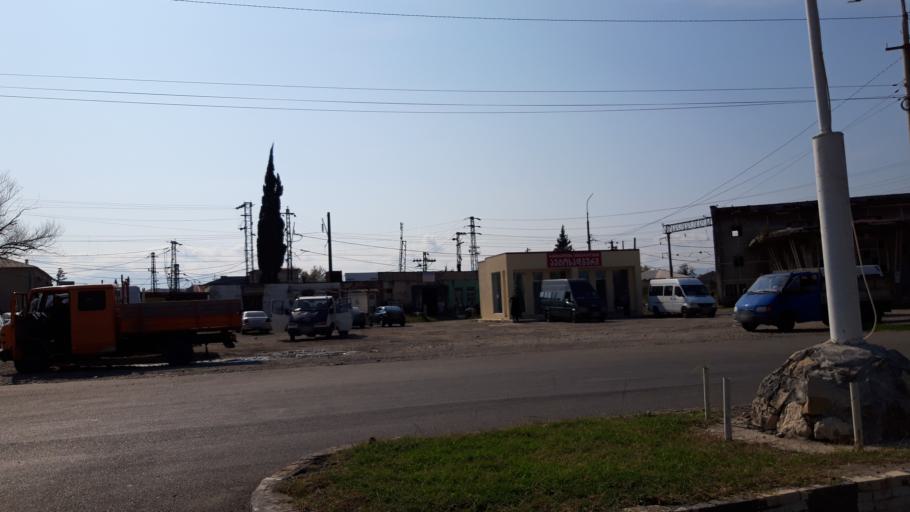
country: GE
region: Imereti
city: Samtredia
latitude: 42.1603
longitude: 42.3367
